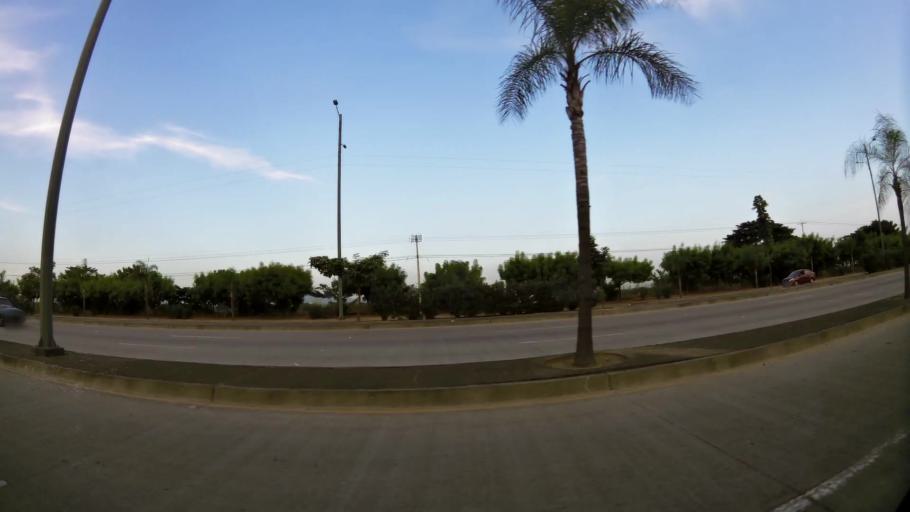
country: EC
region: Guayas
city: Eloy Alfaro
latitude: -2.1066
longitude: -79.8872
